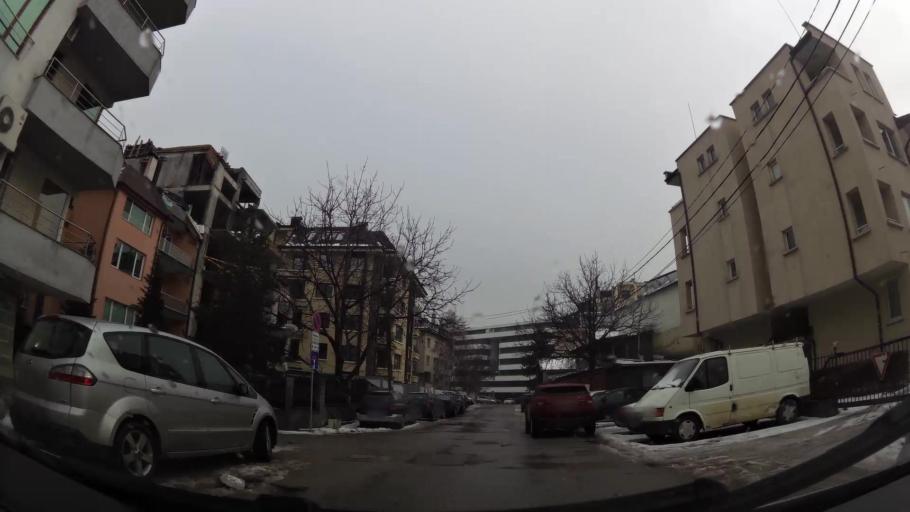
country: BG
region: Sofia-Capital
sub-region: Stolichna Obshtina
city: Sofia
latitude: 42.6613
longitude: 23.2815
